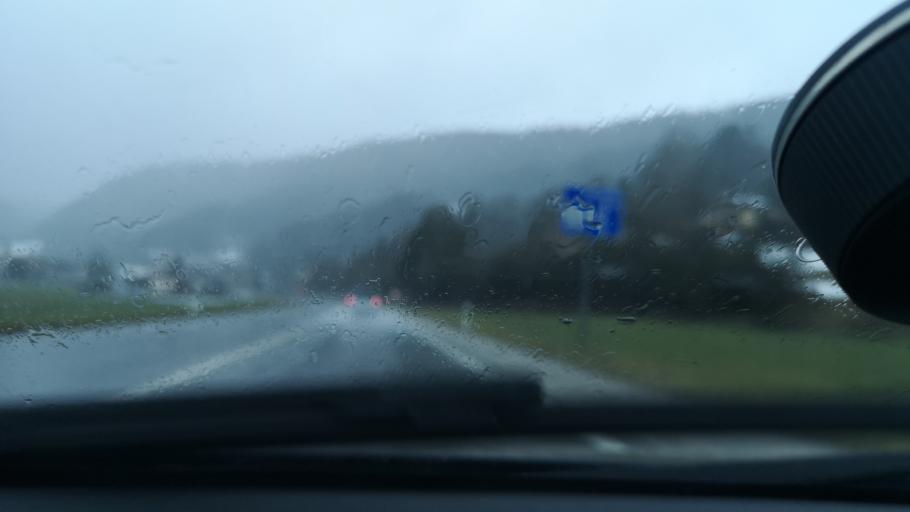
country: CH
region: Neuchatel
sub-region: Val-de-Travers District
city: Couvet
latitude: 46.9189
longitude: 6.6068
